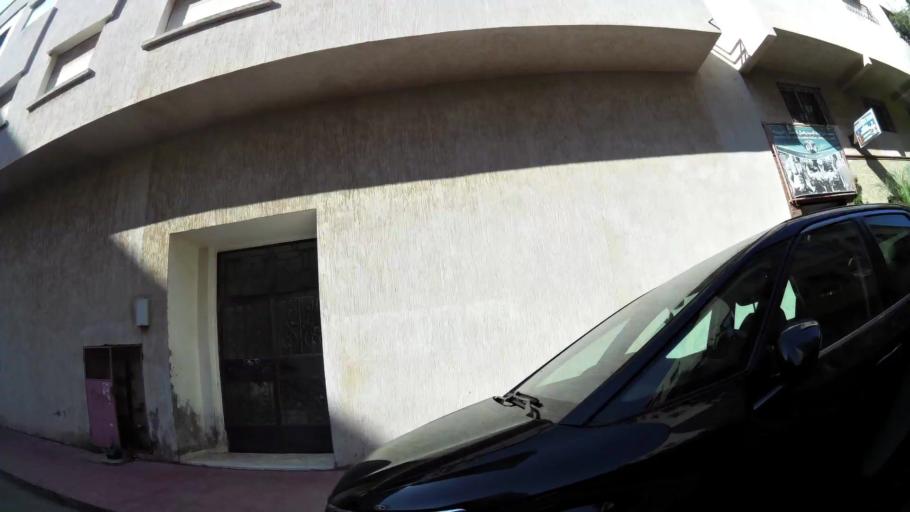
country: MA
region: Rabat-Sale-Zemmour-Zaer
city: Sale
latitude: 34.0483
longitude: -6.8143
